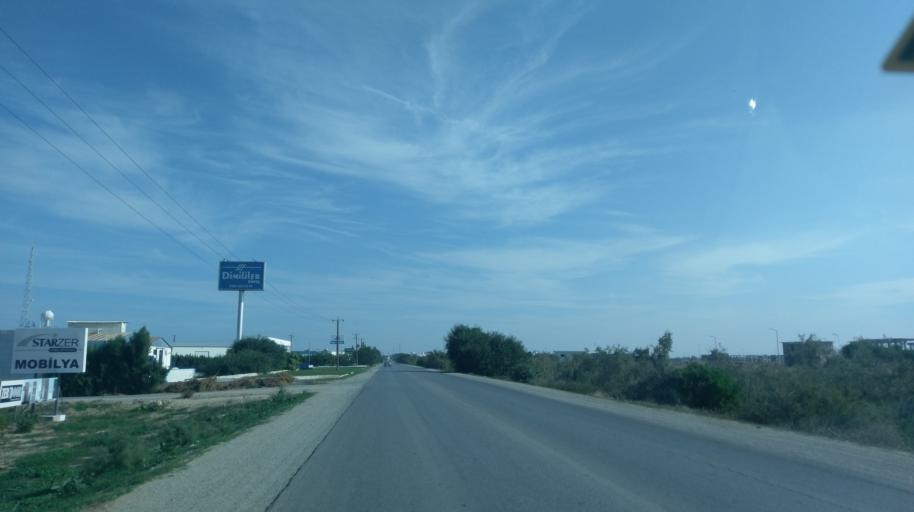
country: CY
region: Ammochostos
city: Acheritou
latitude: 35.1468
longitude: 33.8870
